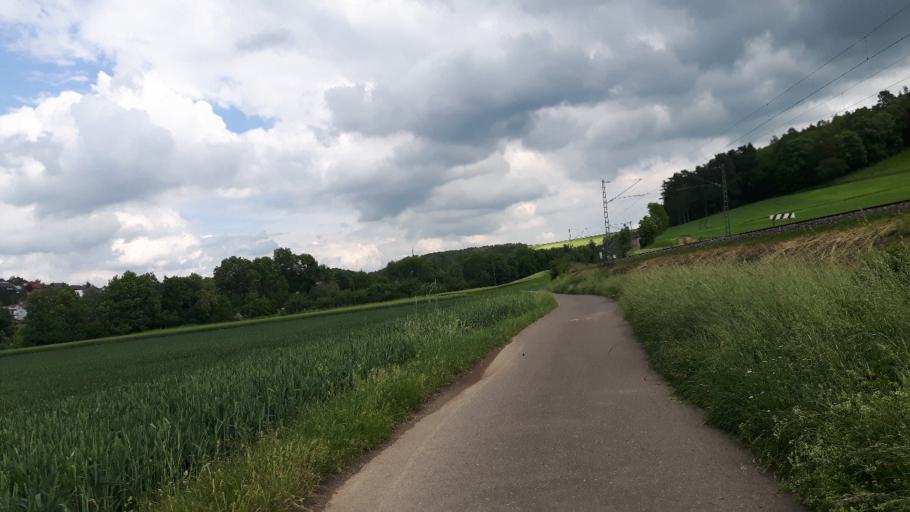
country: DE
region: Baden-Wuerttemberg
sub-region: Regierungsbezirk Stuttgart
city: Grunsfeld
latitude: 49.5978
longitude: 9.7764
